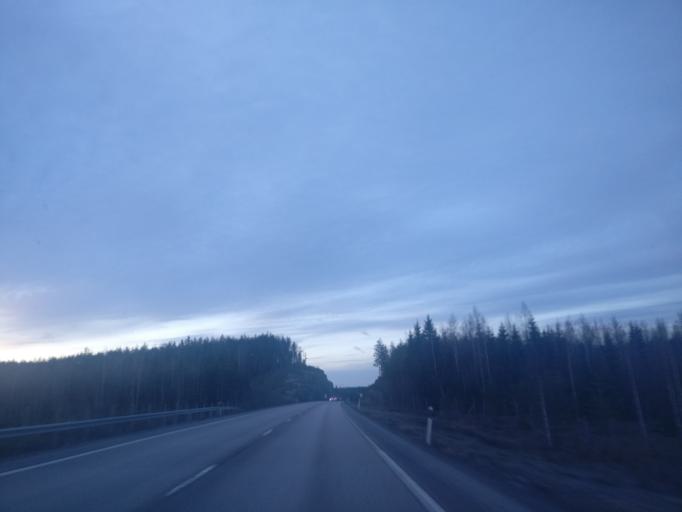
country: FI
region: Central Finland
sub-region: Jyvaeskylae
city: Saeynaetsalo
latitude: 62.2029
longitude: 25.8908
